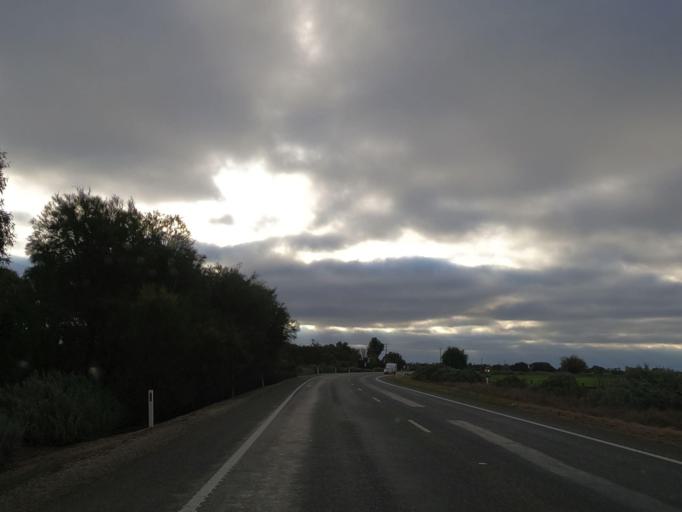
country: AU
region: Victoria
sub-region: Swan Hill
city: Swan Hill
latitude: -35.7221
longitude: 143.8880
